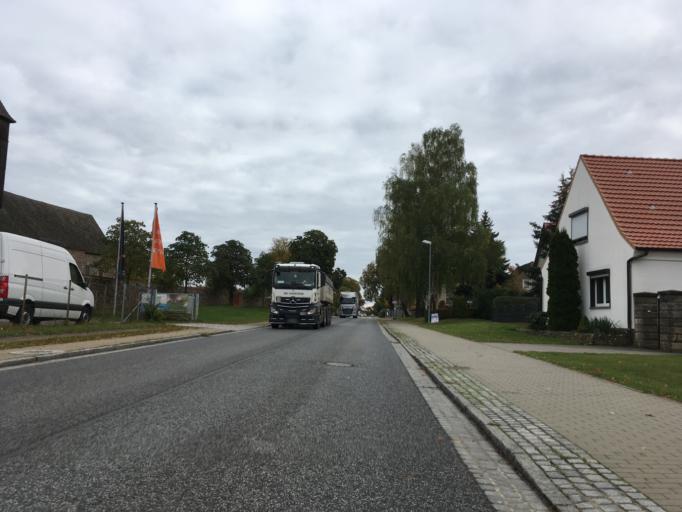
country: DE
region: Brandenburg
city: Werftpfuhl
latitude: 52.7031
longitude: 13.8848
